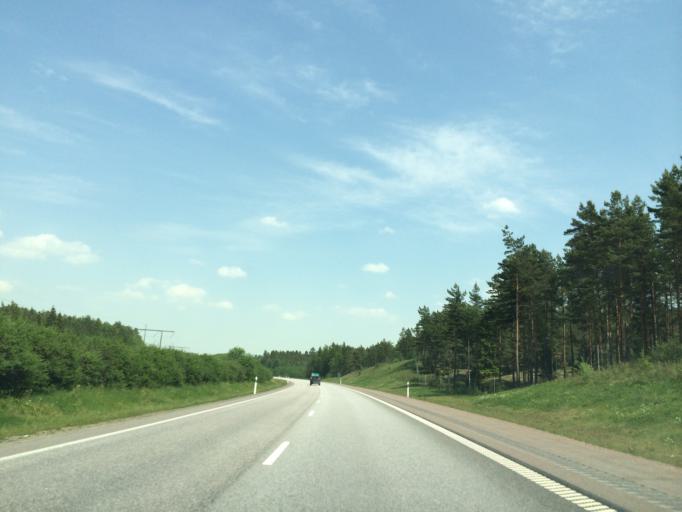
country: SE
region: OEstergoetland
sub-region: Vadstena Kommun
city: Herrestad
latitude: 58.2652
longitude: 14.8531
